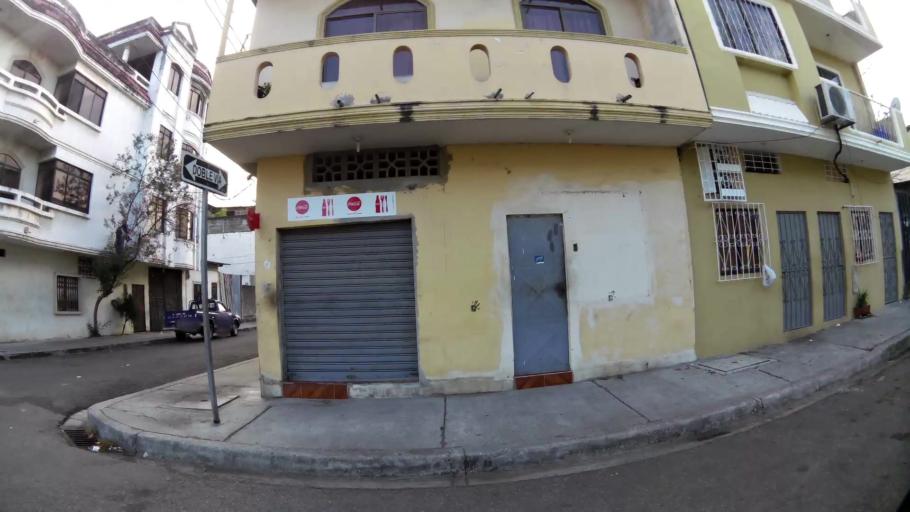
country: EC
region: Guayas
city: Eloy Alfaro
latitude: -2.1351
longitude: -79.8811
